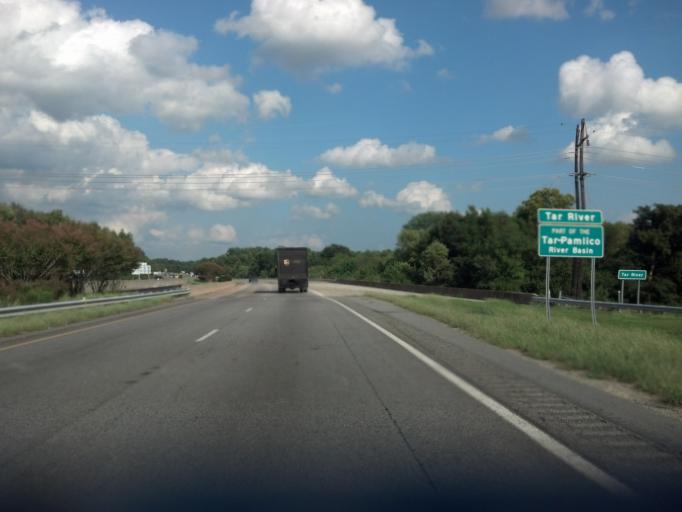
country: US
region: North Carolina
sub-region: Nash County
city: Rocky Mount
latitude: 35.9579
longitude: -77.7832
